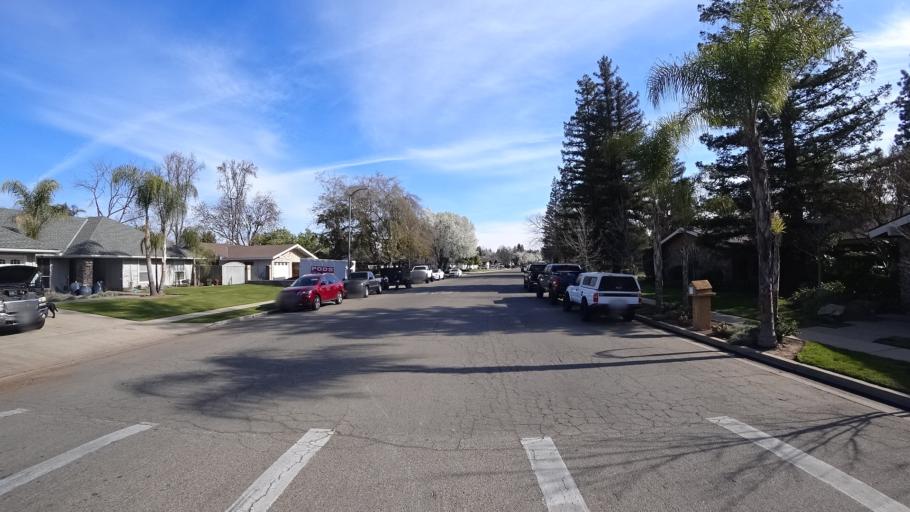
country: US
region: California
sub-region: Fresno County
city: Clovis
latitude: 36.8621
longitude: -119.7785
